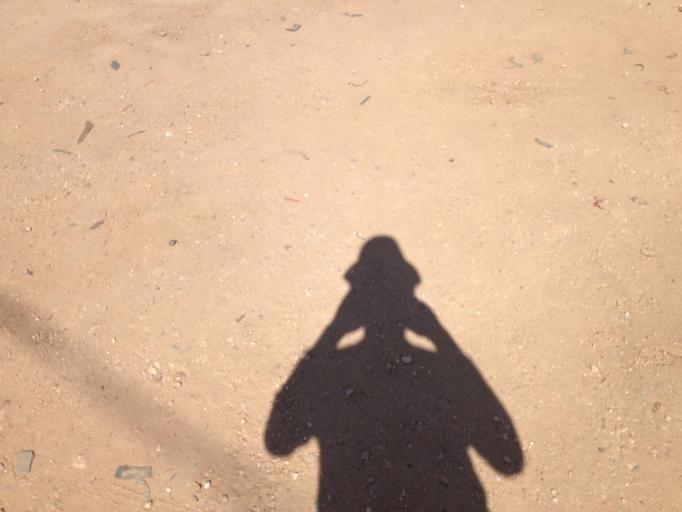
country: CD
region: Katanga
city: Kalemie
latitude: -5.9113
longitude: 29.2083
